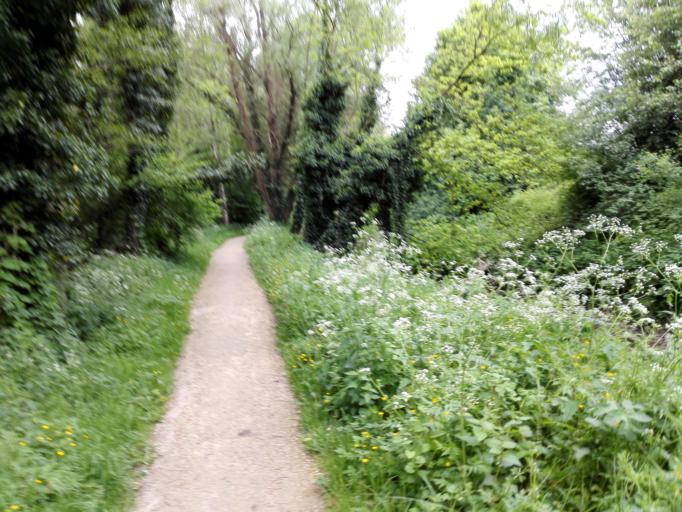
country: BE
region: Flanders
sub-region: Provincie Vlaams-Brabant
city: Huldenberg
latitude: 50.7918
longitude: 4.5963
